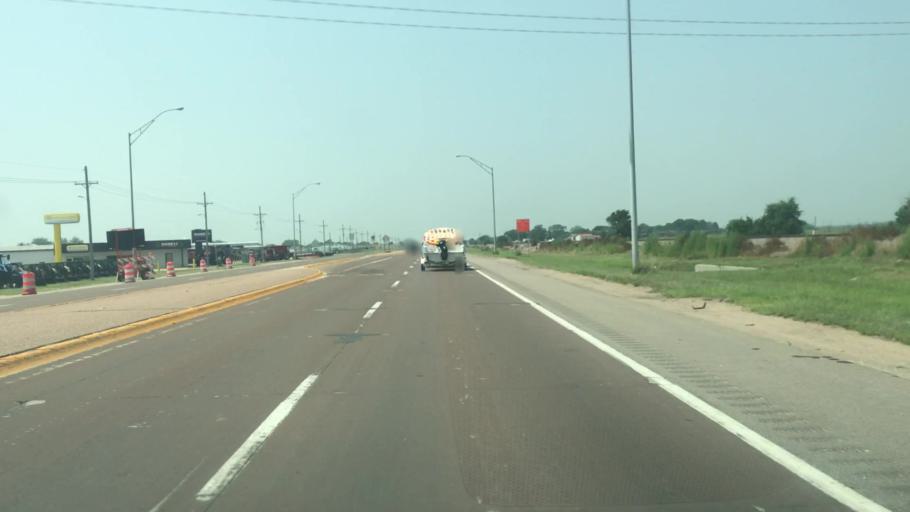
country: US
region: Nebraska
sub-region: Hall County
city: Grand Island
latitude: 40.9544
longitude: -98.3880
